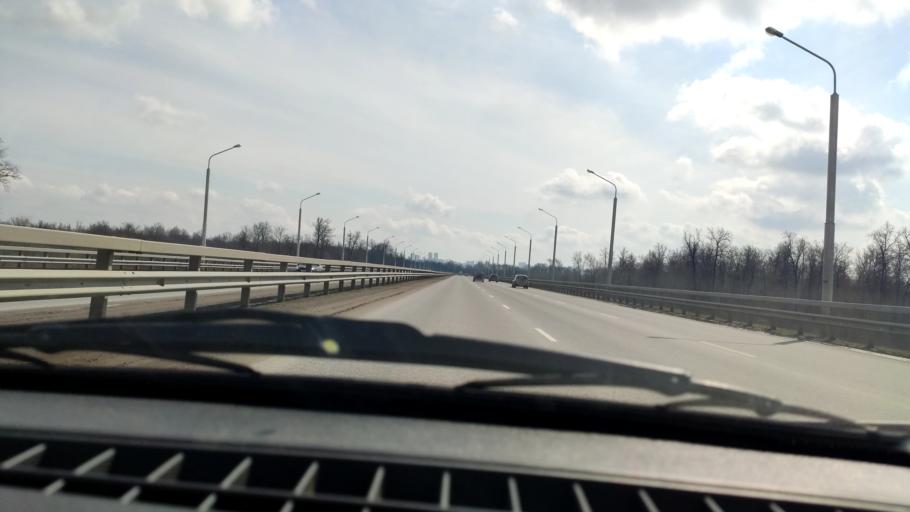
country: RU
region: Bashkortostan
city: Mikhaylovka
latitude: 54.7894
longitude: 55.9078
